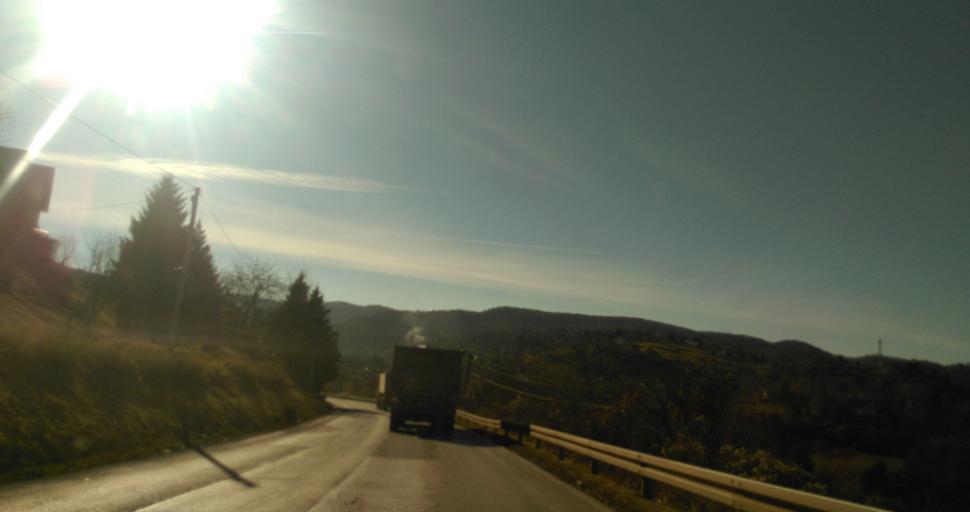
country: RS
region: Autonomna Pokrajina Vojvodina
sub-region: Juznobacki Okrug
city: Novi Sad
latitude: 45.2044
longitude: 19.8426
